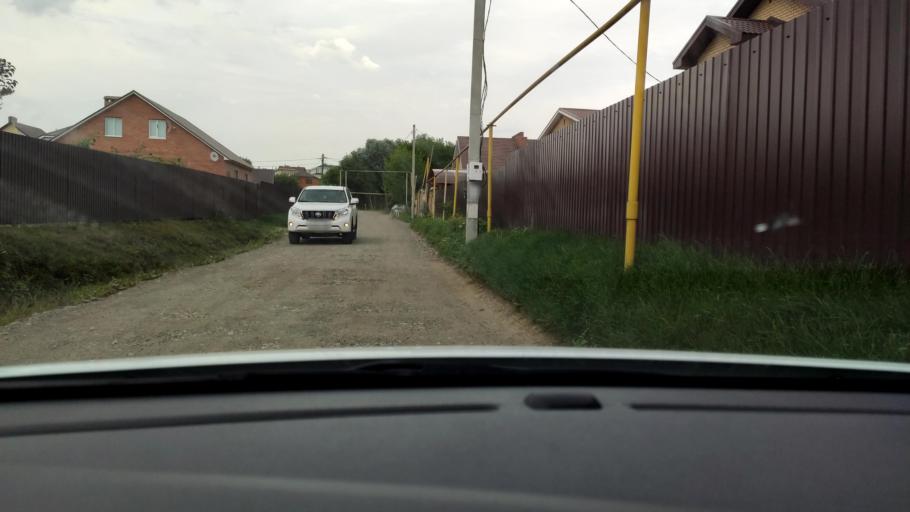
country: RU
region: Tatarstan
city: Stolbishchi
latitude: 55.7620
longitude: 49.2562
